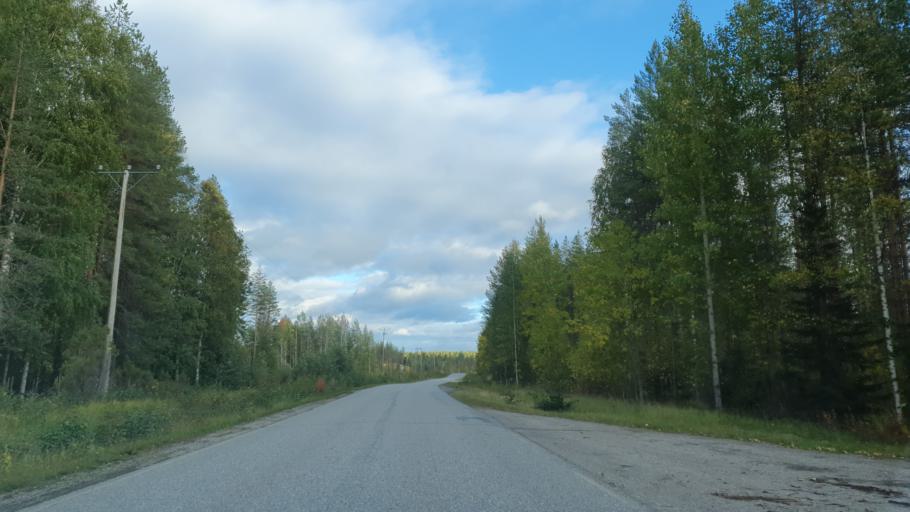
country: FI
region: Kainuu
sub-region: Kehys-Kainuu
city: Kuhmo
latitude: 63.9291
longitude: 29.9977
